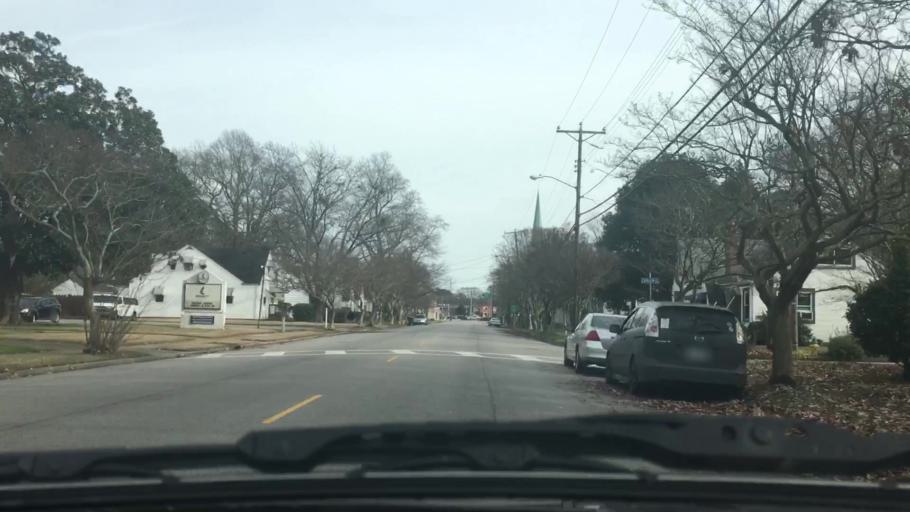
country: US
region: Virginia
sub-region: City of Norfolk
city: Norfolk
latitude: 36.8899
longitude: -76.2428
